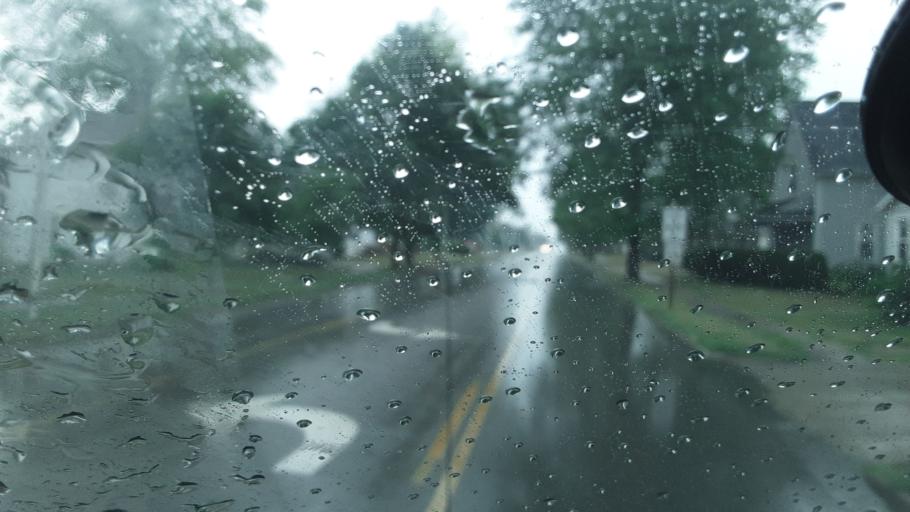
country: US
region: Ohio
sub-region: Williams County
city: Montpelier
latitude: 41.5865
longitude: -84.6033
